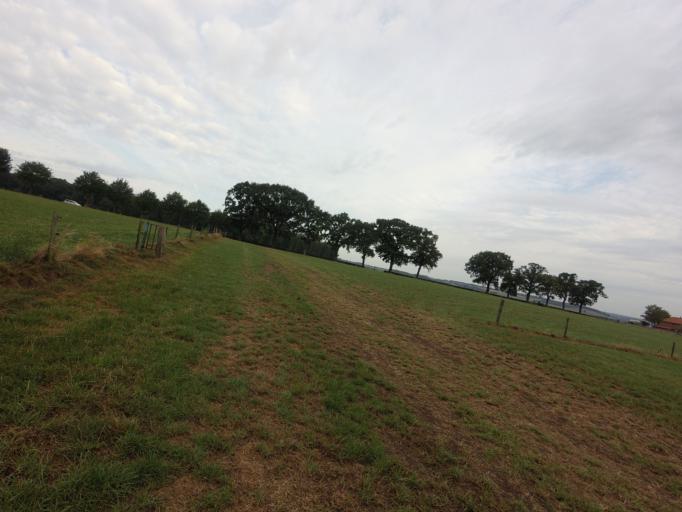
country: NL
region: Limburg
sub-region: Valkenburg aan de Geul
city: Schin op Geul
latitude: 50.7969
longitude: 5.8879
